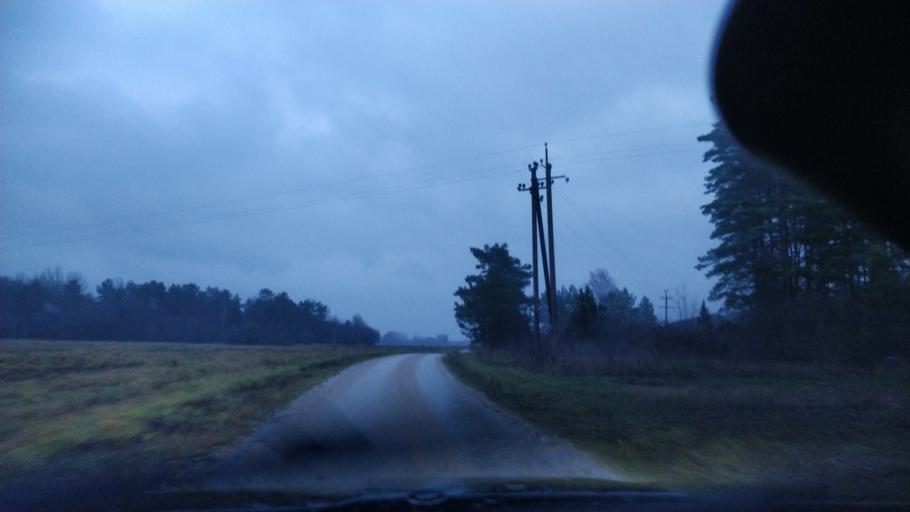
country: EE
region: Laeaene
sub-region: Lihula vald
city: Lihula
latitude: 58.8519
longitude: 23.9938
